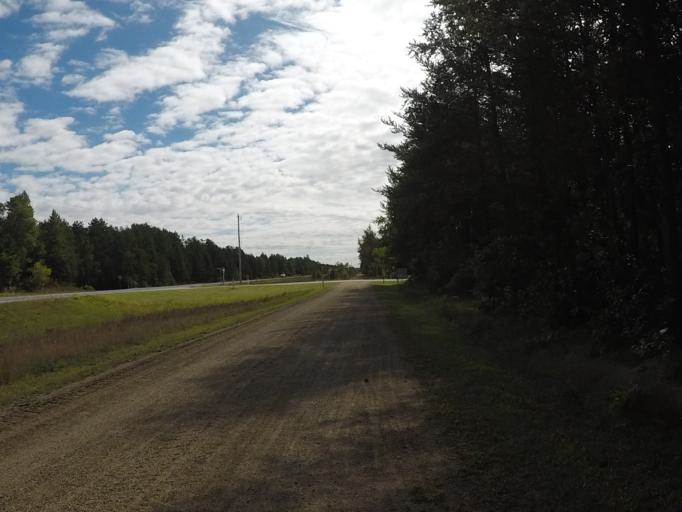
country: US
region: Wisconsin
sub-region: Richland County
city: Richland Center
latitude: 43.2152
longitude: -90.2827
